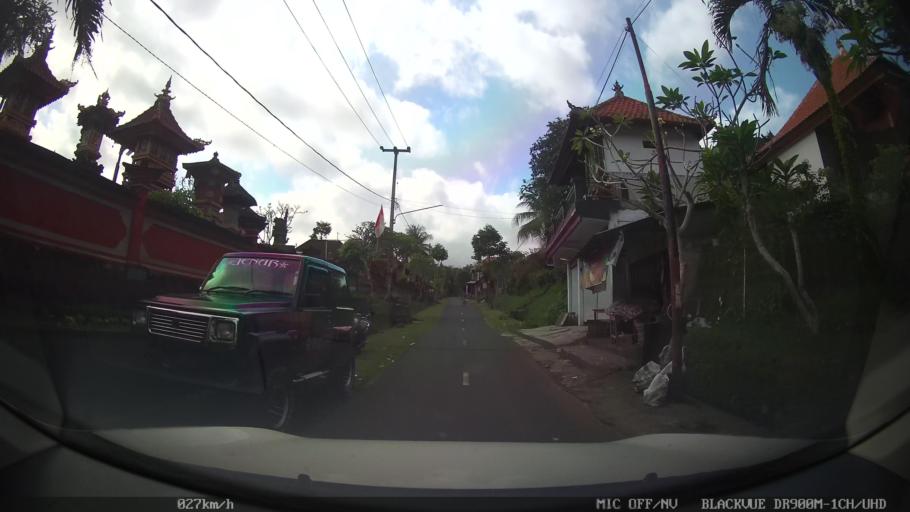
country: ID
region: Bali
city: Banjar Pesalakan
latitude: -8.5146
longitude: 115.3060
